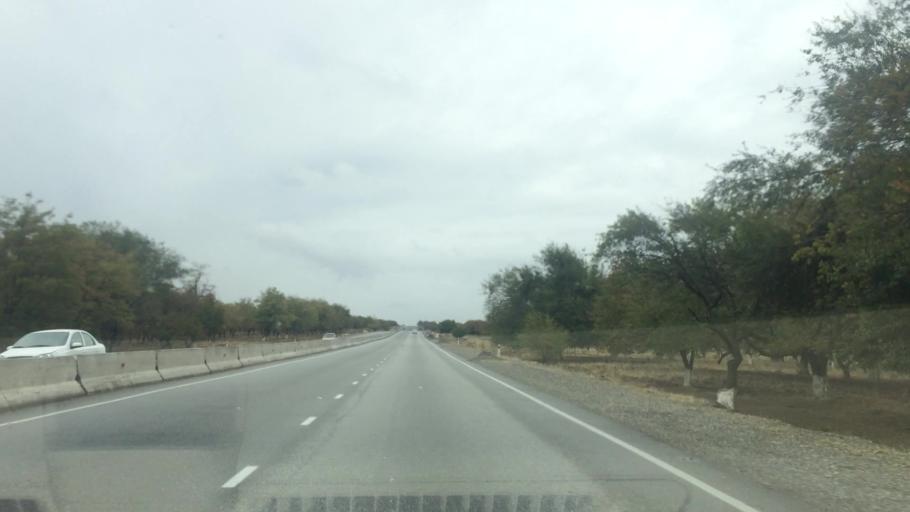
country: UZ
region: Samarqand
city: Bulung'ur
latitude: 39.8684
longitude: 67.4762
